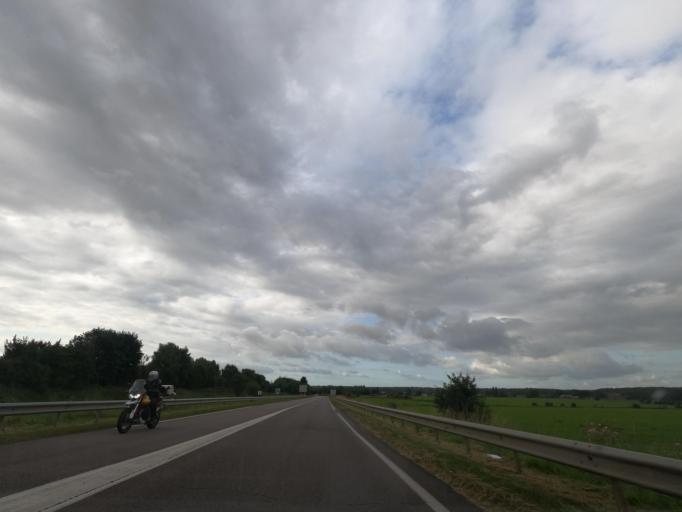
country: FR
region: Haute-Normandie
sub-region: Departement de l'Eure
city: Bourgtheroulde-Infreville
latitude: 49.2993
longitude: 0.8844
